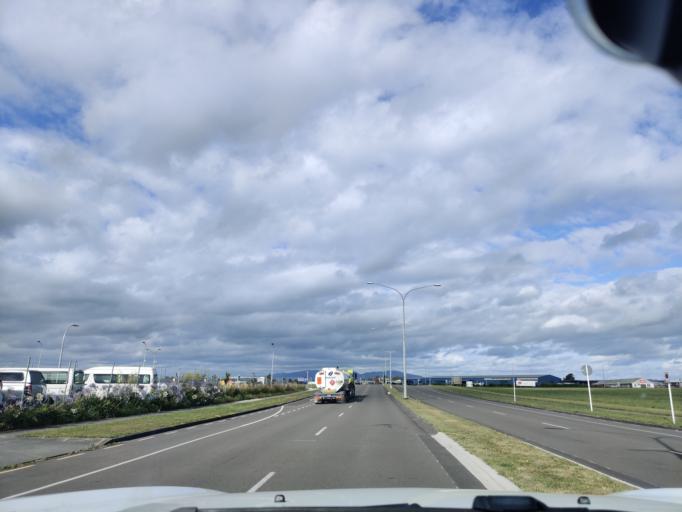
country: NZ
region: Manawatu-Wanganui
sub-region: Palmerston North City
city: Palmerston North
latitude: -40.3255
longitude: 175.6223
